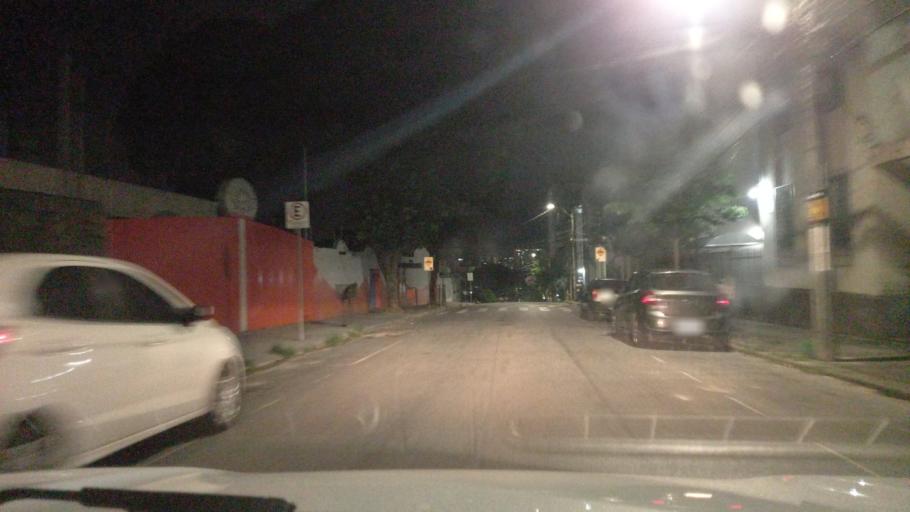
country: BR
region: Minas Gerais
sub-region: Belo Horizonte
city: Belo Horizonte
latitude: -19.8891
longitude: -43.9255
